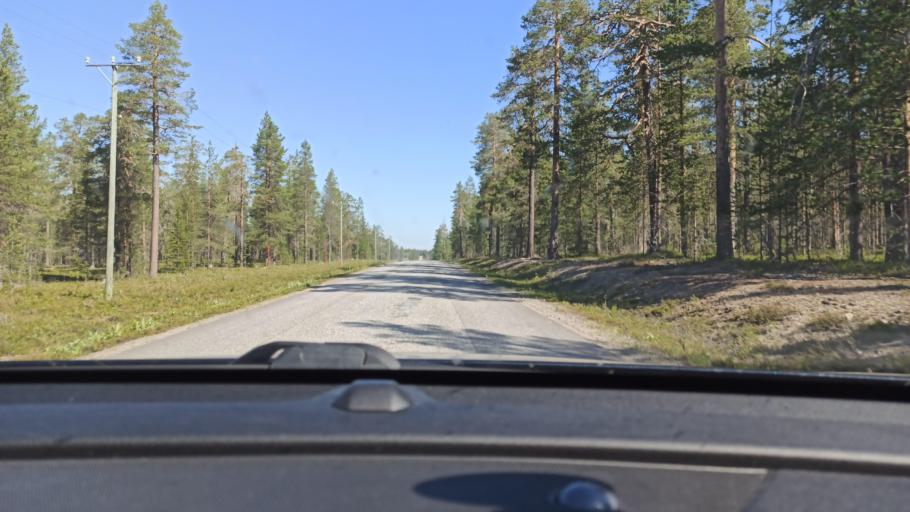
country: FI
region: Lapland
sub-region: Tunturi-Lappi
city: Kolari
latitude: 67.6413
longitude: 24.1581
